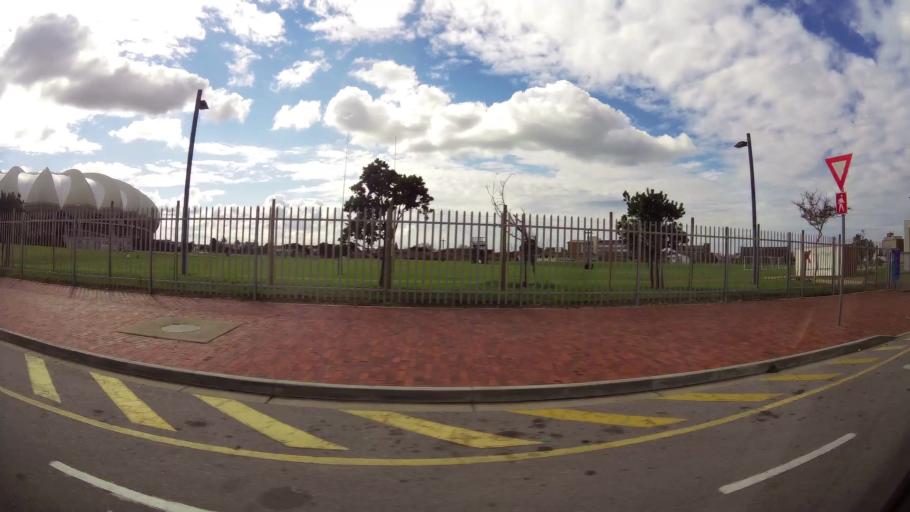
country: ZA
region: Eastern Cape
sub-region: Nelson Mandela Bay Metropolitan Municipality
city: Port Elizabeth
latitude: -33.9409
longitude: 25.6002
